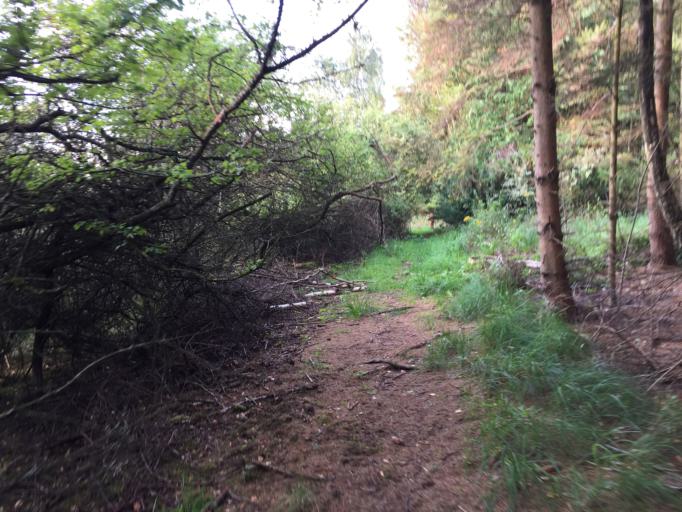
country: DK
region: Capital Region
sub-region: Fureso Kommune
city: Farum
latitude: 55.8270
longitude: 12.3640
